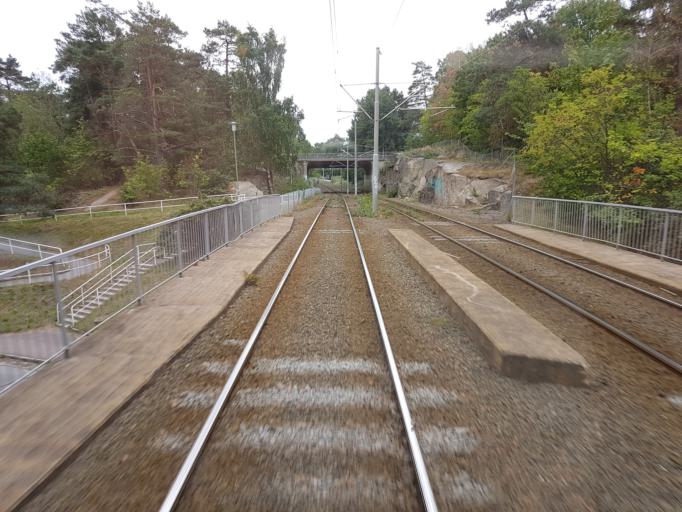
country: SE
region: Vaestra Goetaland
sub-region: Goteborg
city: Majorna
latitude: 57.6688
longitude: 11.9247
